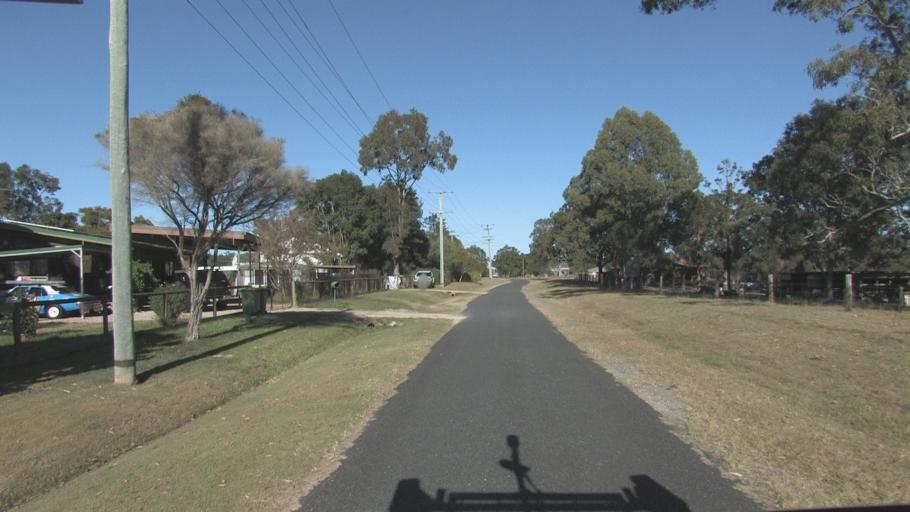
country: AU
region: Queensland
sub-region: Logan
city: Chambers Flat
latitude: -27.7597
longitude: 153.0527
